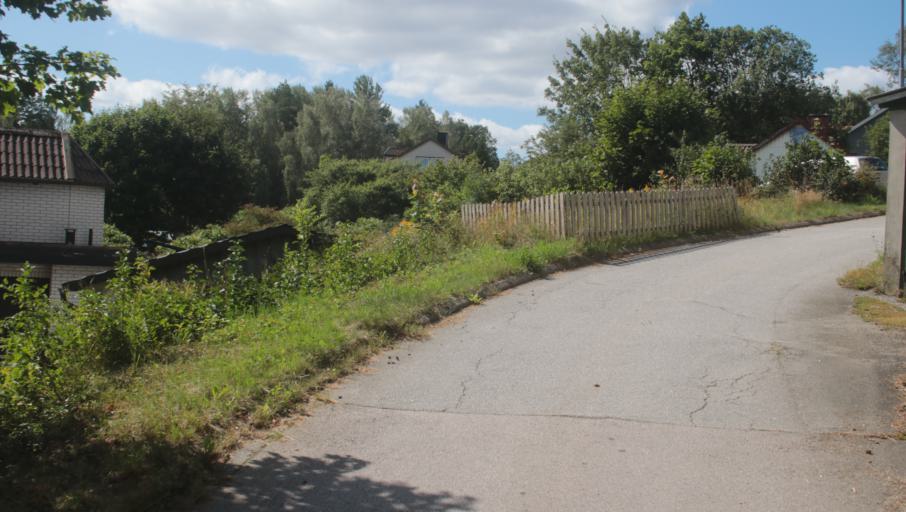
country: SE
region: Blekinge
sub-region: Karlshamns Kommun
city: Svangsta
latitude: 56.2582
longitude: 14.7701
